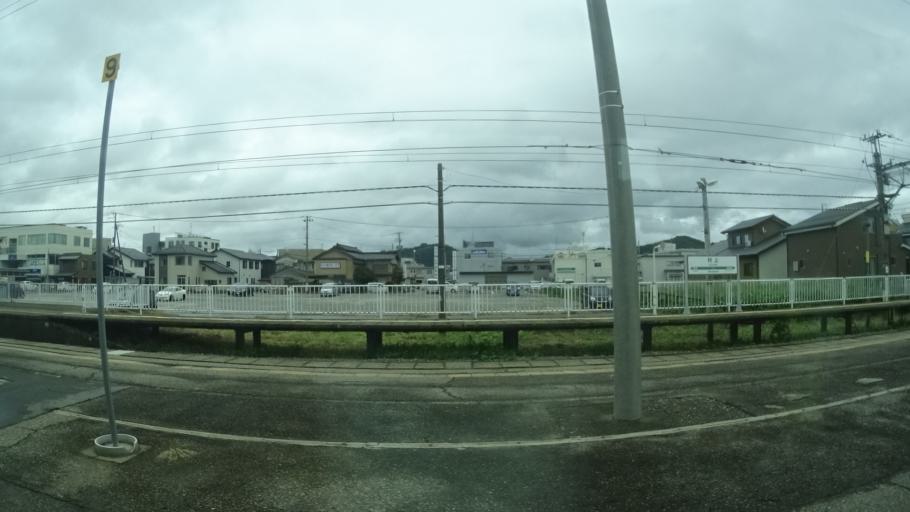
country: JP
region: Niigata
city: Murakami
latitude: 38.2193
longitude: 139.4633
